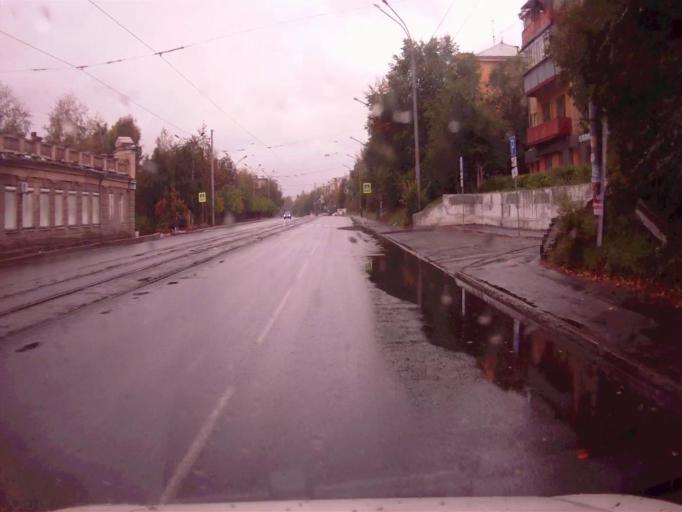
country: RU
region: Chelyabinsk
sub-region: Gorod Chelyabinsk
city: Chelyabinsk
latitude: 55.1830
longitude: 61.4145
